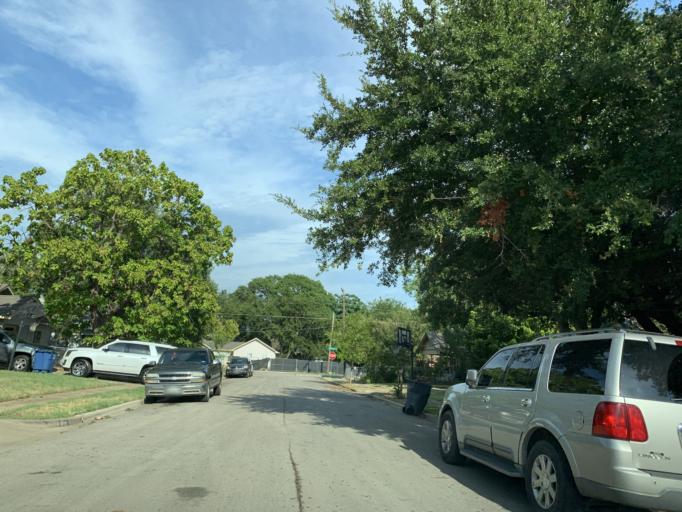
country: US
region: Texas
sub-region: Dallas County
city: Dallas
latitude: 32.7373
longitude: -96.8329
